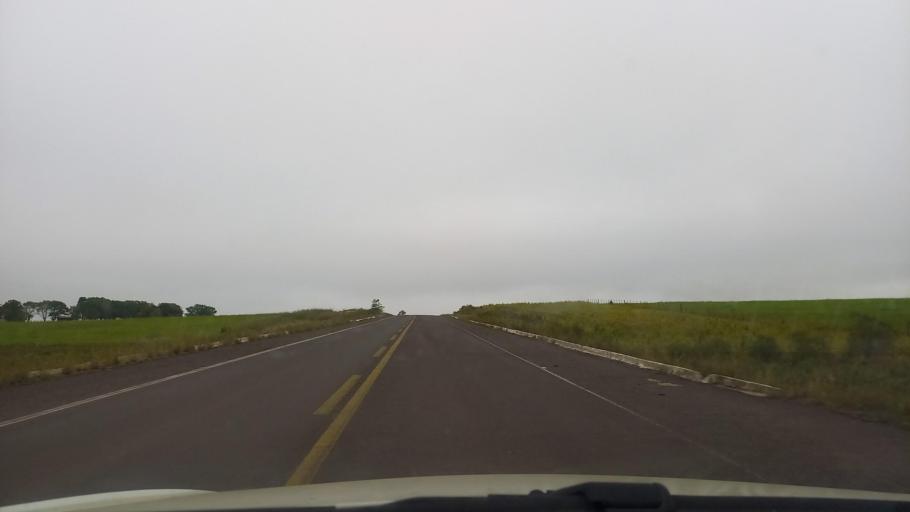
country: BR
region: Rio Grande do Sul
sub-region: Cacequi
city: Cacequi
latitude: -30.0451
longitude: -54.5958
